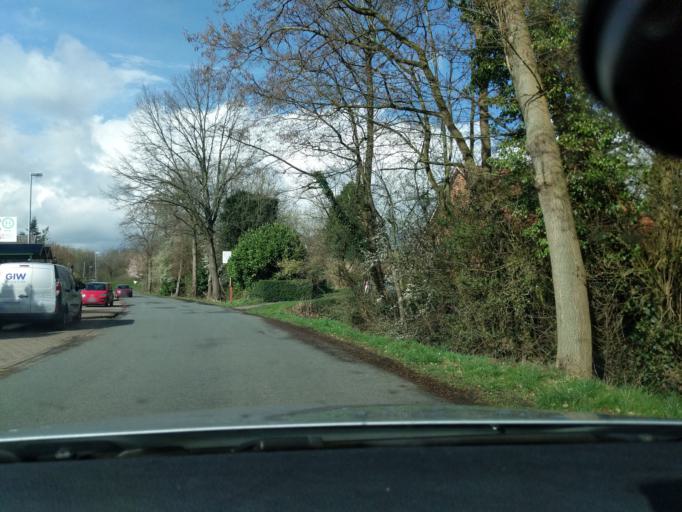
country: DE
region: Lower Saxony
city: Stade
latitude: 53.6126
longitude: 9.5075
